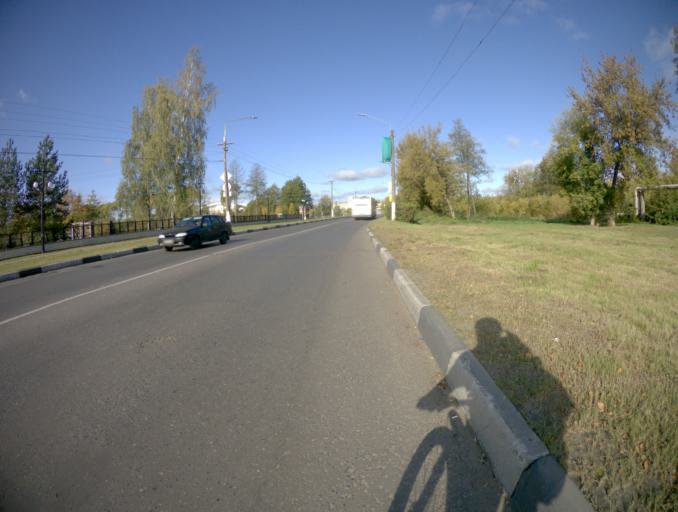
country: RU
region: Moskovskaya
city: Roshal'
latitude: 55.6626
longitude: 39.8681
